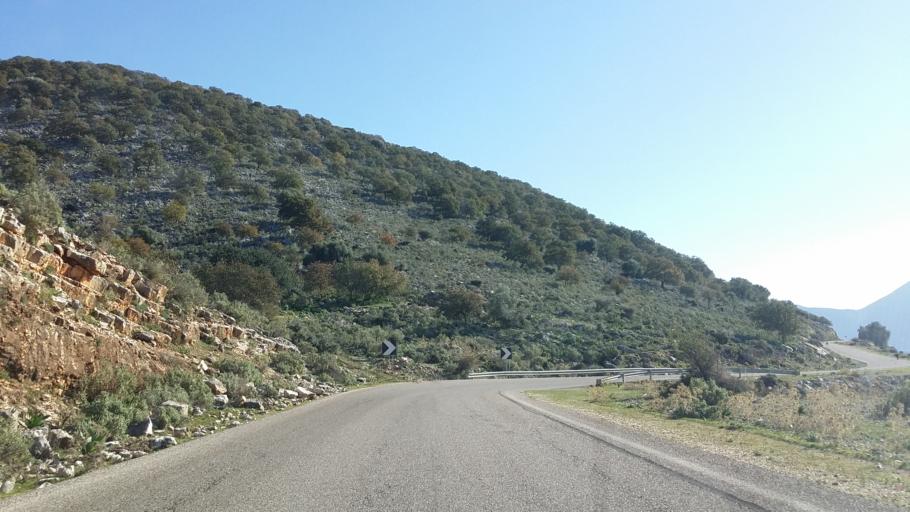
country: GR
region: West Greece
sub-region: Nomos Aitolias kai Akarnanias
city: Kandila
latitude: 38.7047
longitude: 20.8973
